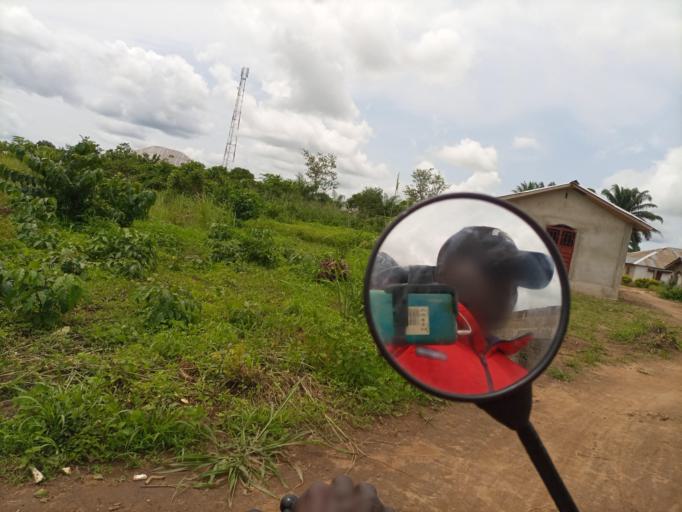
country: SL
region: Southern Province
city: Bo
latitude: 7.9640
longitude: -11.7169
